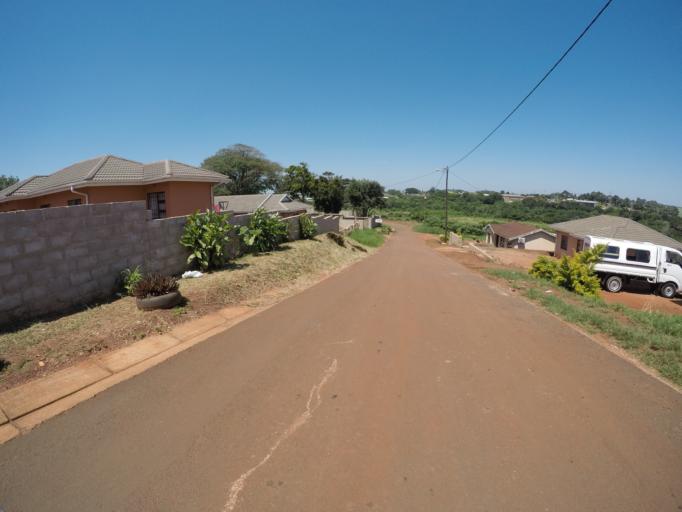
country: ZA
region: KwaZulu-Natal
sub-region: uThungulu District Municipality
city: Empangeni
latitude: -28.7736
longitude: 31.8836
